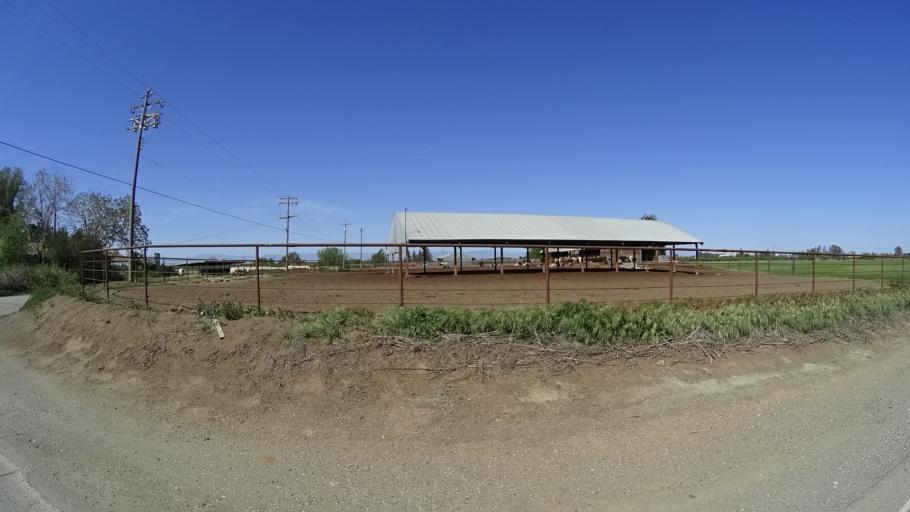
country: US
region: California
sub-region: Glenn County
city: Hamilton City
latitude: 39.7395
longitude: -122.1043
